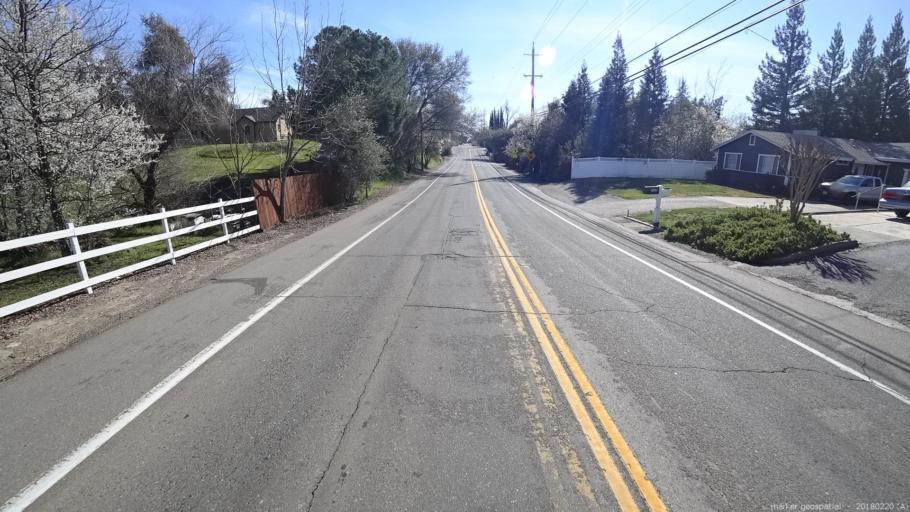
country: US
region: California
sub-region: Sacramento County
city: Orangevale
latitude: 38.6992
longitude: -121.2016
